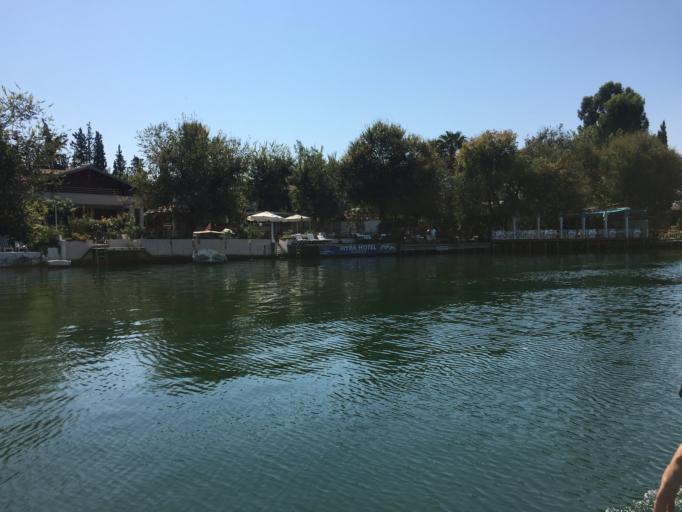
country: TR
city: Dalyan
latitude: 36.8293
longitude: 28.6369
